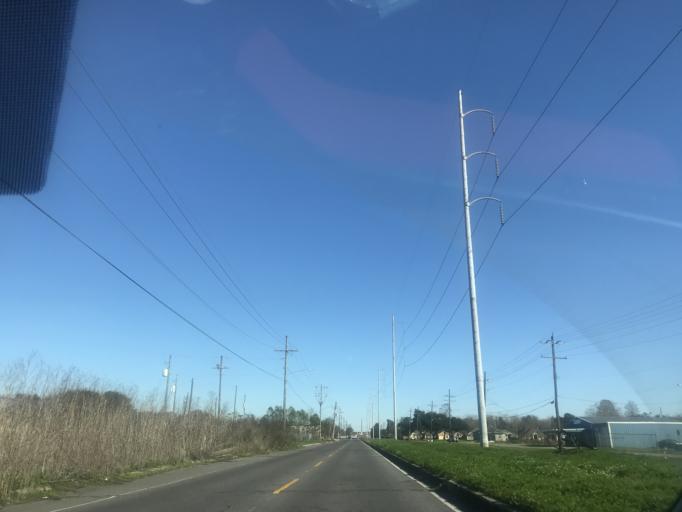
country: US
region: Louisiana
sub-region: Saint Bernard Parish
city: Arabi
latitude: 30.0238
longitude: -89.9918
